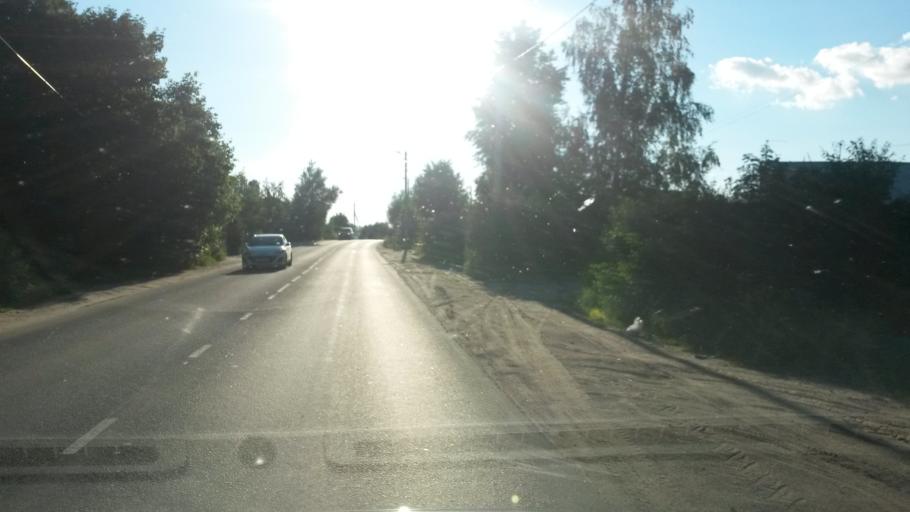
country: RU
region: Ivanovo
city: Novo-Talitsy
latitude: 57.0205
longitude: 40.9161
